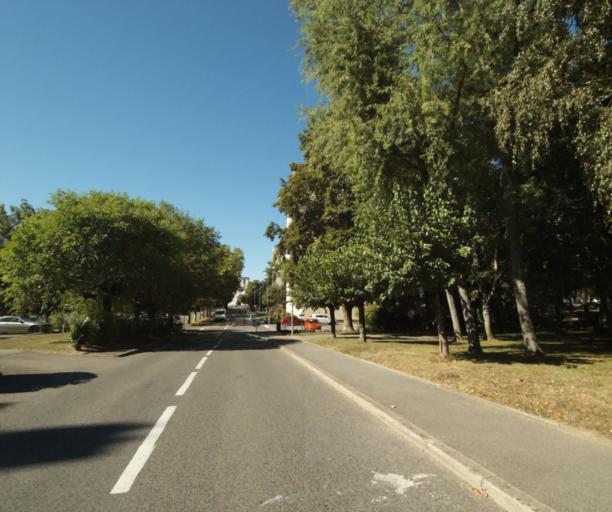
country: FR
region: Rhone-Alpes
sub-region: Departement de l'Ain
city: Ferney-Voltaire
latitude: 46.2594
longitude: 6.1107
